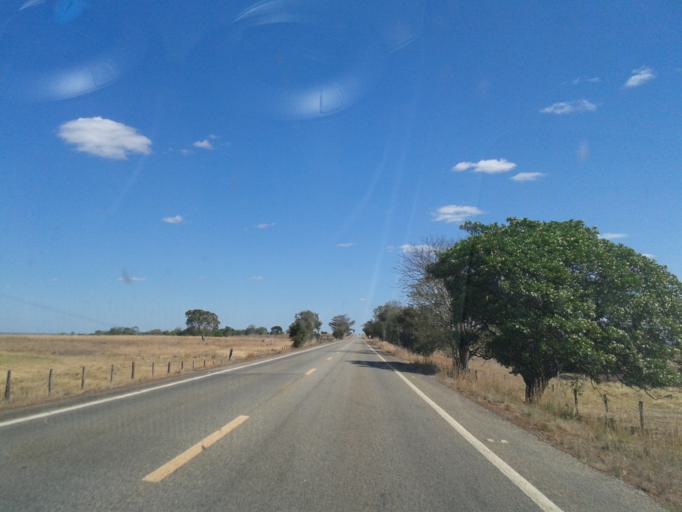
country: BR
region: Goias
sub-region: Sao Miguel Do Araguaia
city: Sao Miguel do Araguaia
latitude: -13.4077
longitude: -50.2637
